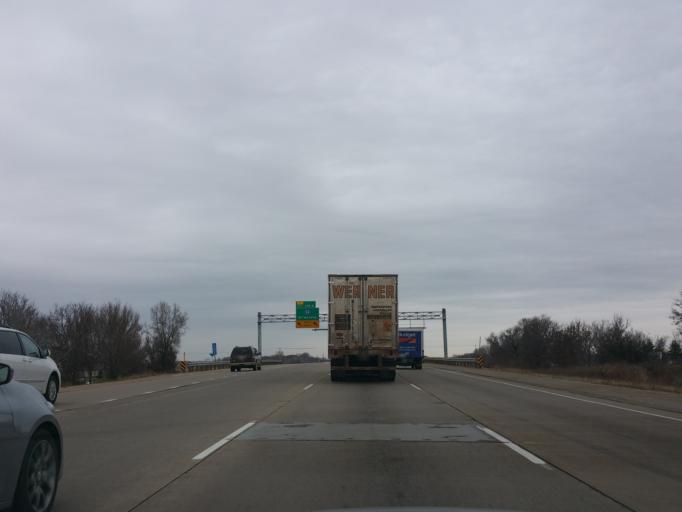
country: US
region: Wisconsin
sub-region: Dane County
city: Monona
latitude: 43.1107
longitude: -89.2859
